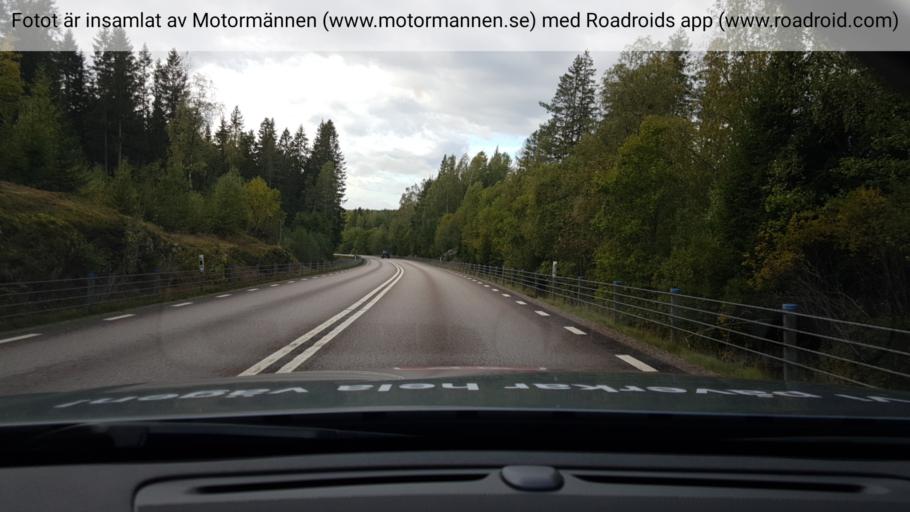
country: SE
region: Vaermland
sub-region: Arjangs Kommun
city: Toecksfors
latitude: 59.4981
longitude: 11.9025
